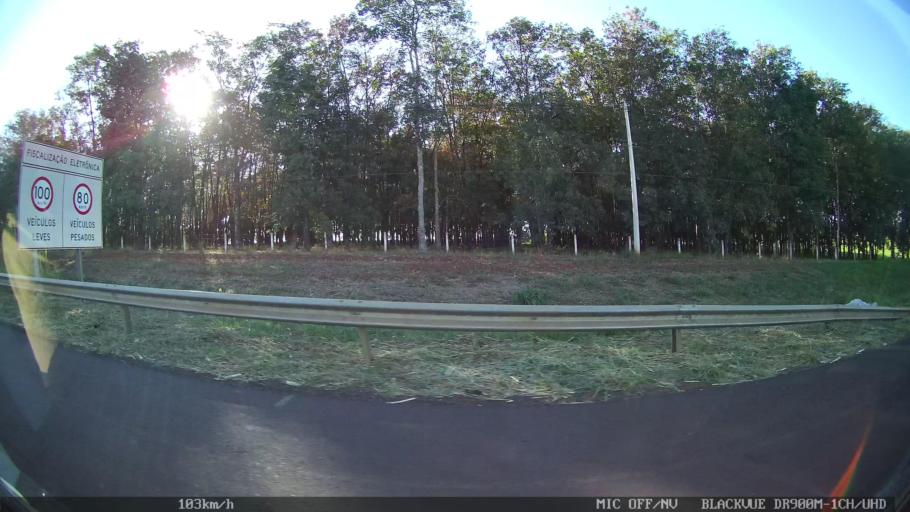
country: BR
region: Sao Paulo
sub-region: Olimpia
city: Olimpia
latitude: -20.7252
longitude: -49.0340
